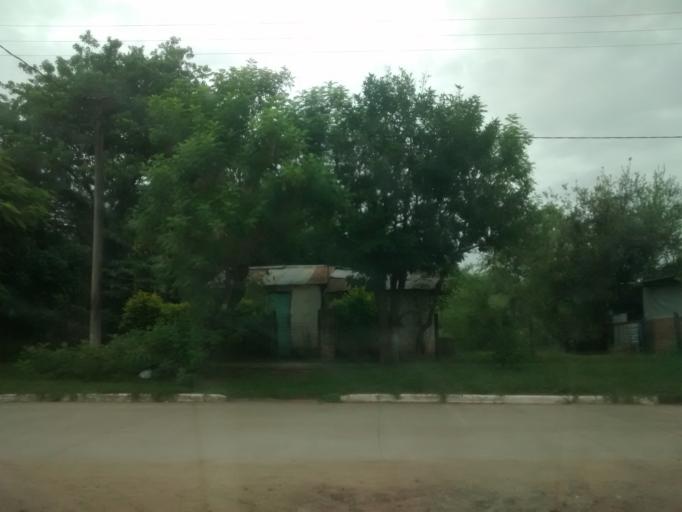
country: AR
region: Chaco
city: Puerto Tirol
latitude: -27.3704
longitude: -59.0930
